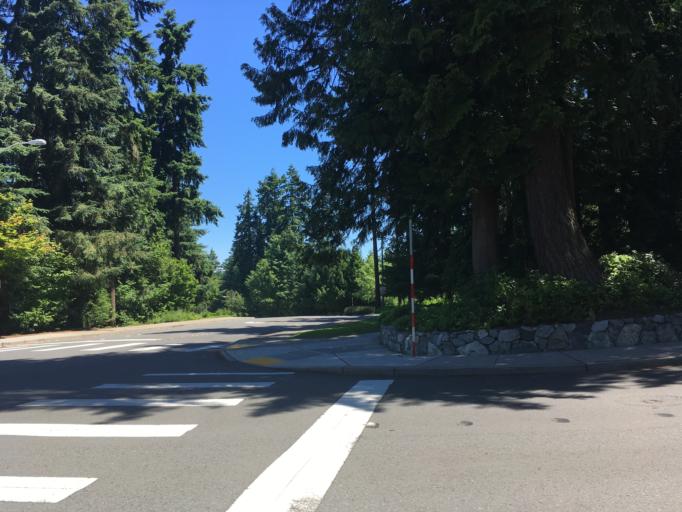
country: US
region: Washington
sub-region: King County
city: Redmond
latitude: 47.6421
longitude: -122.1254
